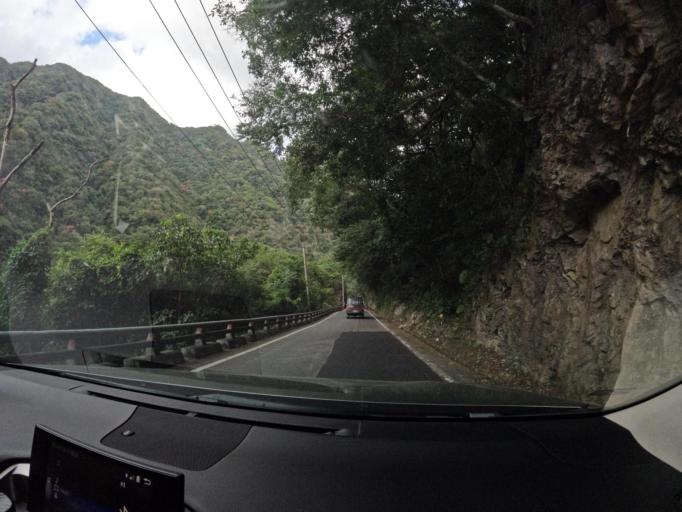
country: TW
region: Taiwan
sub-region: Taitung
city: Taitung
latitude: 23.1418
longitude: 121.0975
